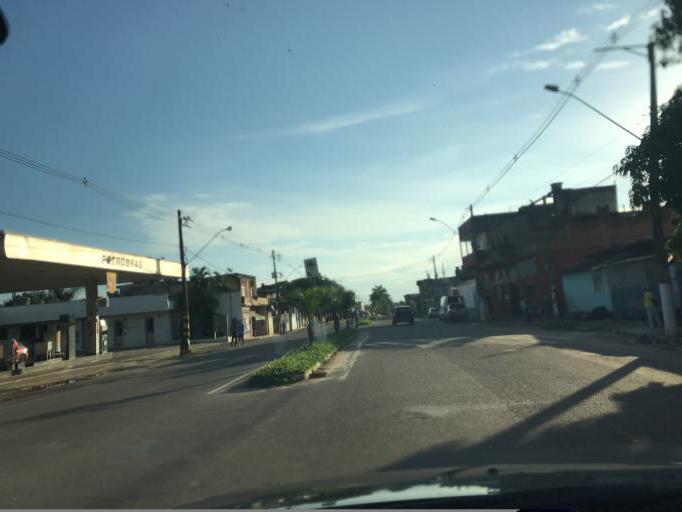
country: BR
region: Minas Gerais
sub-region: Tres Coracoes
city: Tres Coracoes
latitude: -21.6908
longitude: -45.2391
